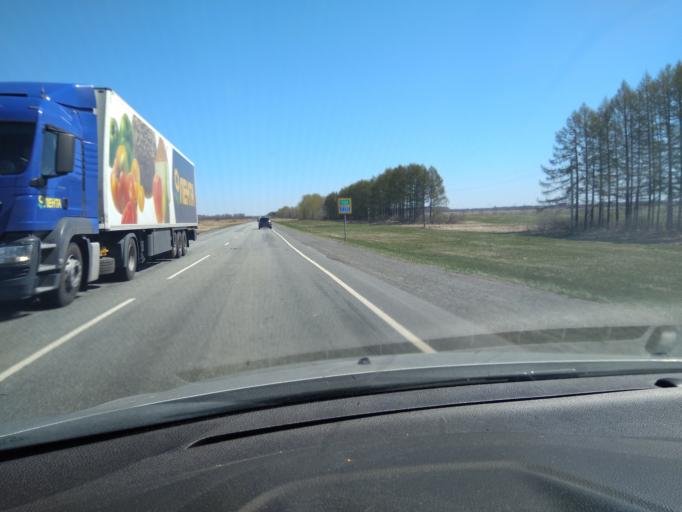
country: RU
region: Sverdlovsk
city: Talitsa
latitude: 57.0591
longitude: 63.5363
